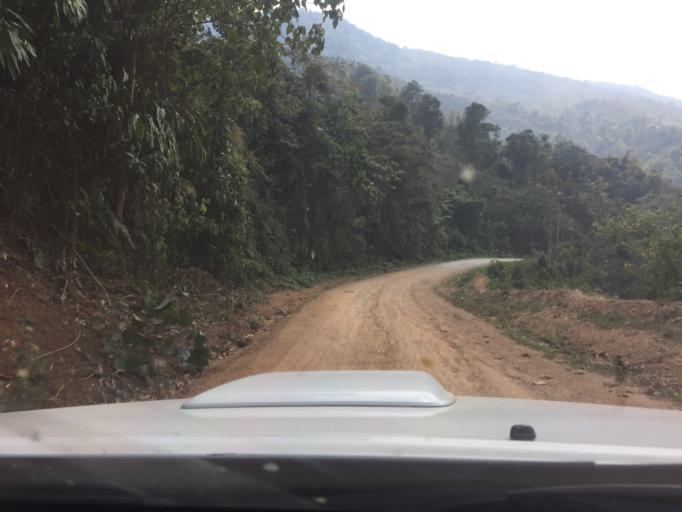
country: TH
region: Nan
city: Song Khwae
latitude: 19.7455
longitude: 100.7010
